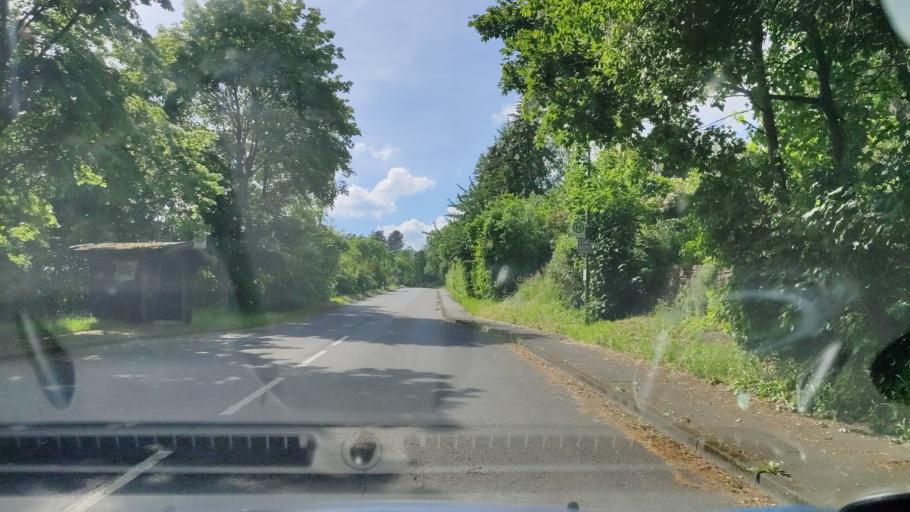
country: DE
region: Lower Saxony
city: Rosdorf
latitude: 51.5347
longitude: 9.8500
